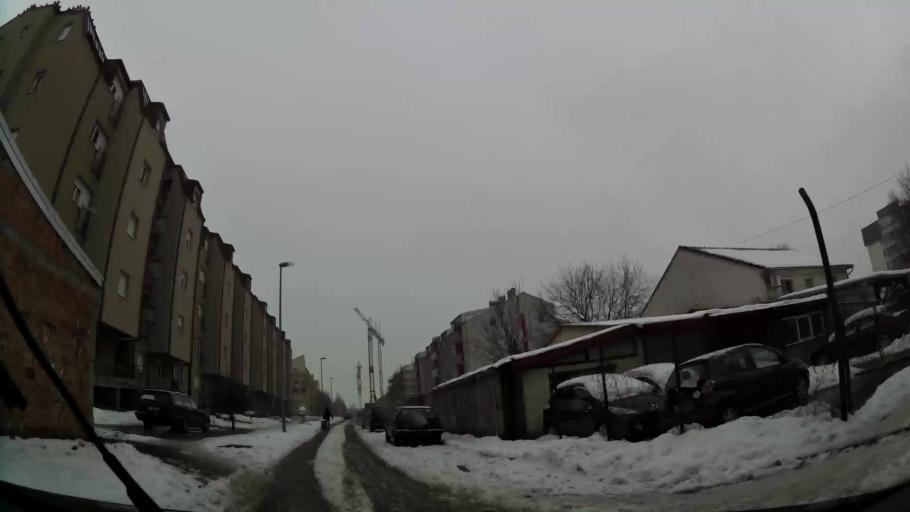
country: RS
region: Central Serbia
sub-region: Belgrade
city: Zemun
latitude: 44.8742
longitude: 20.3268
